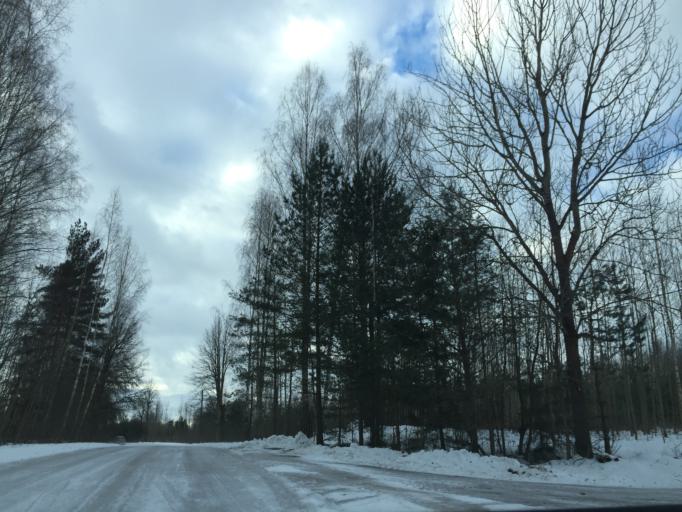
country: LV
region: Lielvarde
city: Lielvarde
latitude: 56.5742
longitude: 24.7352
